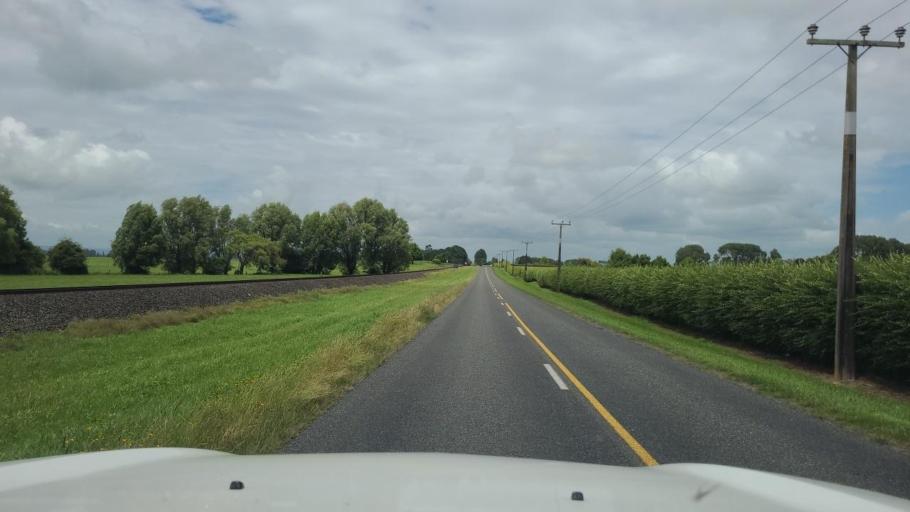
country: NZ
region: Waikato
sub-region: Matamata-Piako District
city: Matamata
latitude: -37.8704
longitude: 175.7564
